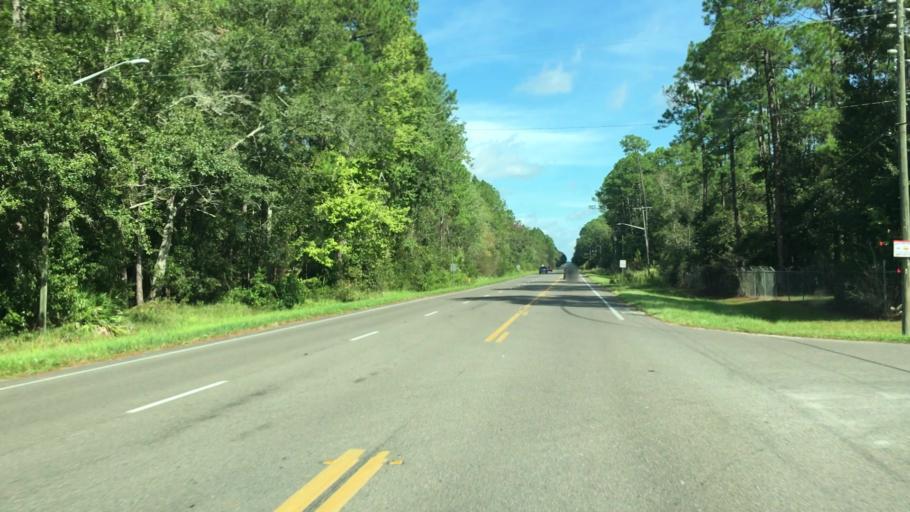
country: US
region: Florida
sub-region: Alachua County
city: Gainesville
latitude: 29.7060
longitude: -82.2774
